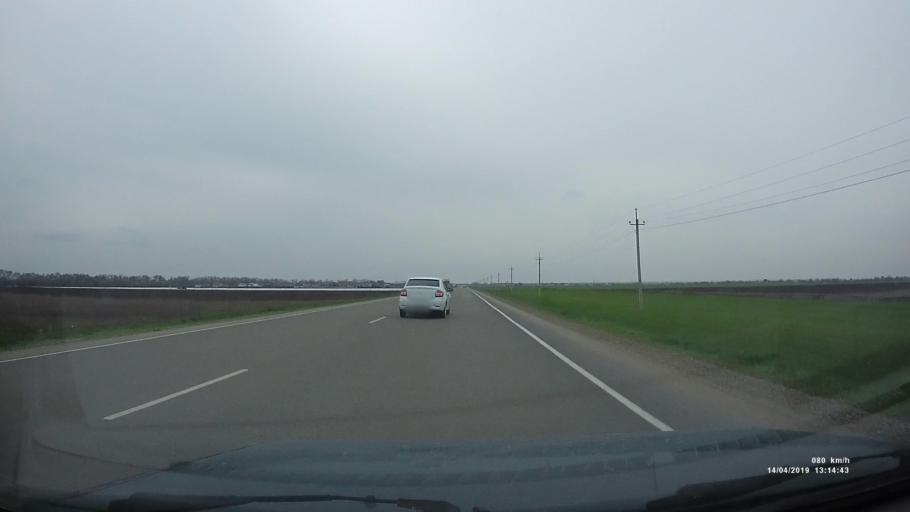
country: RU
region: Rostov
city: Kuleshovka
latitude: 47.0888
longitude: 39.6052
